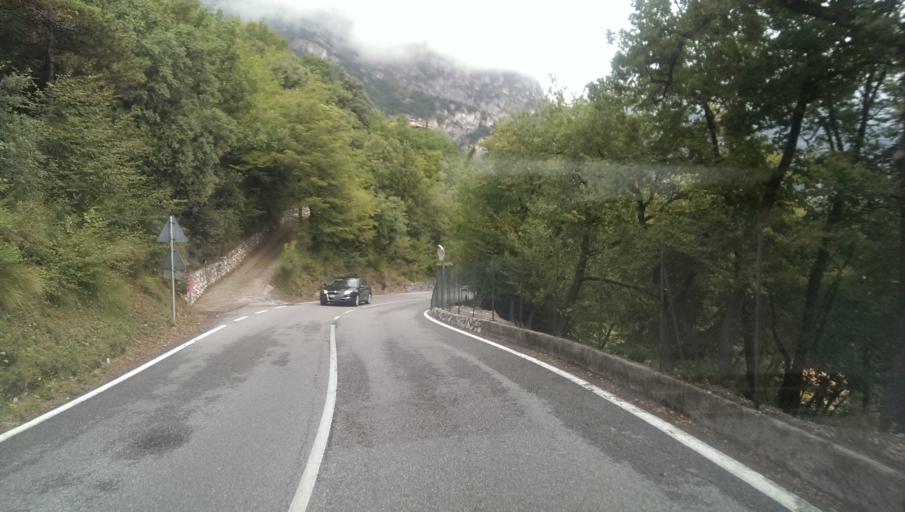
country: IT
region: Lombardy
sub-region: Provincia di Brescia
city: Limone sul Garda
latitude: 45.7976
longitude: 10.7811
